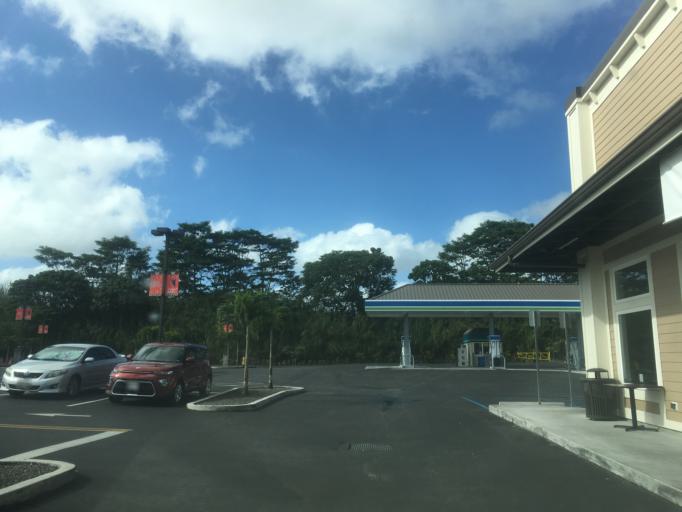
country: US
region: Hawaii
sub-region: Hawaii County
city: Hawaiian Paradise Park
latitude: 19.5029
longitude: -154.9570
